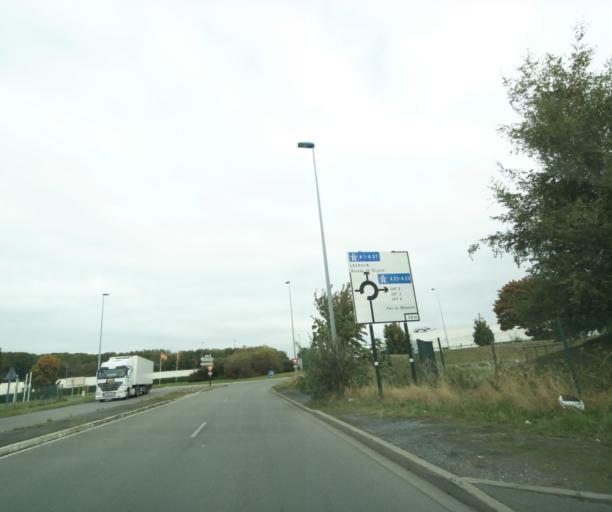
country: FR
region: Nord-Pas-de-Calais
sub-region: Departement du Nord
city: Lesquin
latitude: 50.5760
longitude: 3.1128
